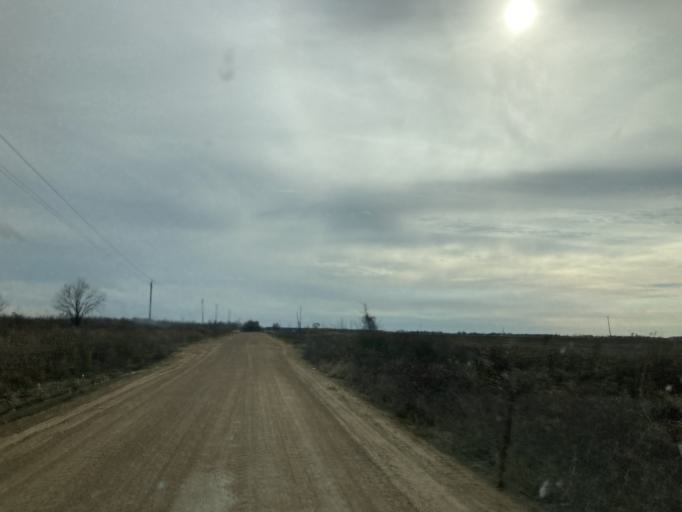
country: US
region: Mississippi
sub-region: Humphreys County
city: Belzoni
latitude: 33.1696
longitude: -90.5723
